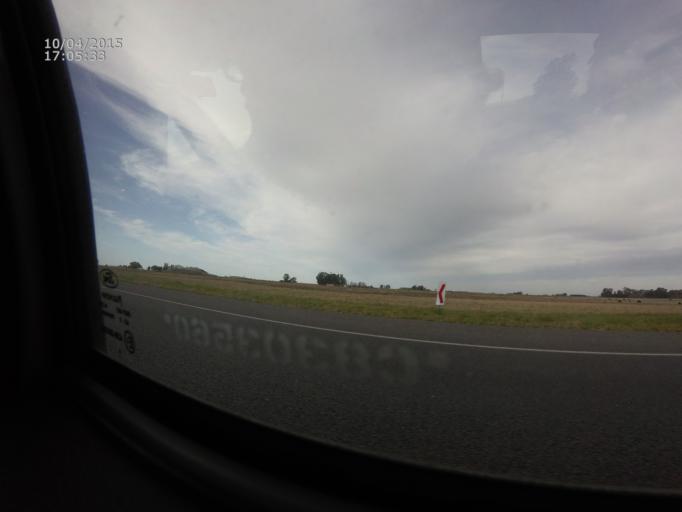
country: AR
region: Buenos Aires
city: Coronel Vidal
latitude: -37.3819
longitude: -57.7479
